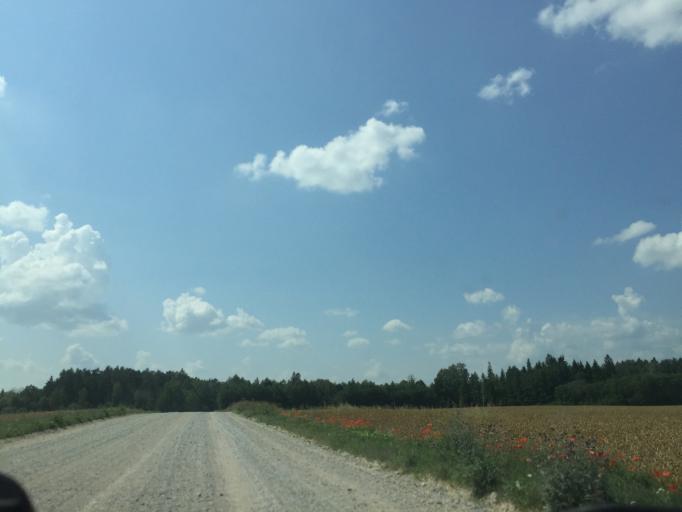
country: LT
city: Zagare
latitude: 56.3887
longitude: 23.3080
